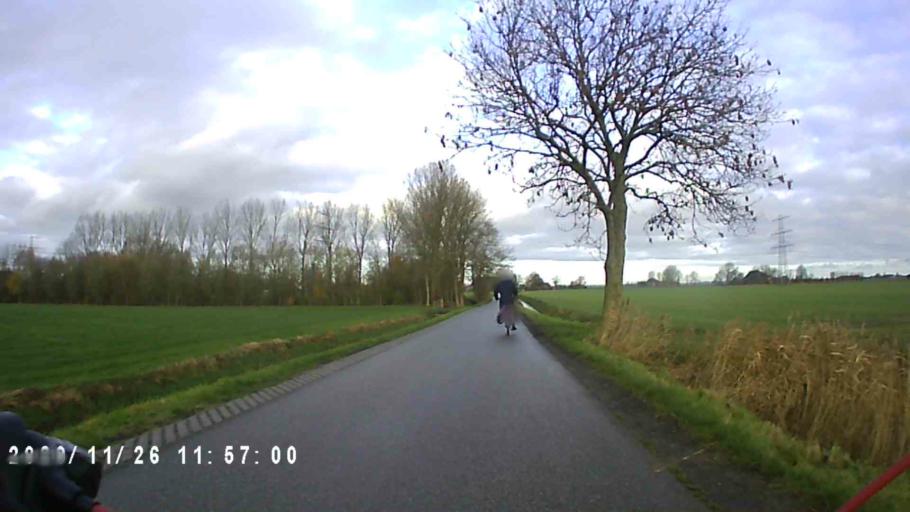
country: NL
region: Groningen
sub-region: Gemeente Bedum
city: Bedum
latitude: 53.3093
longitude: 6.6036
